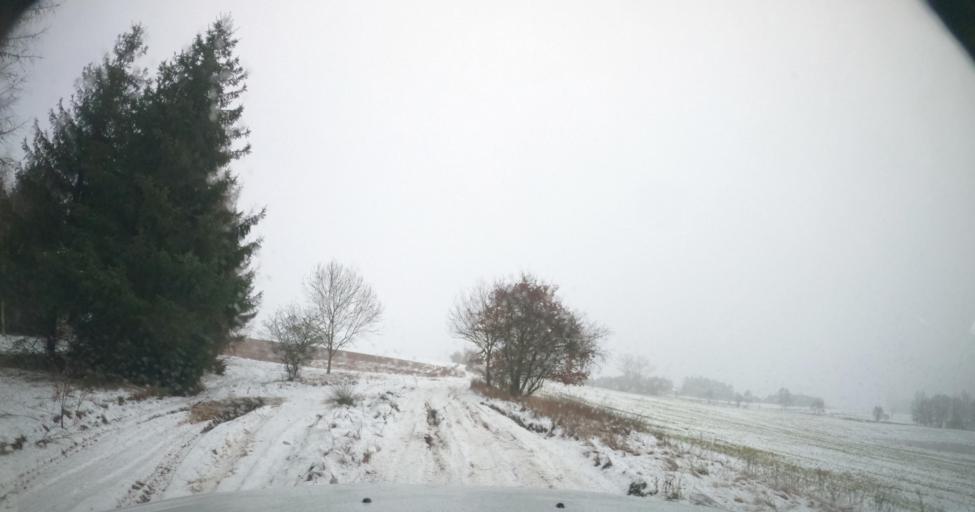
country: PL
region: West Pomeranian Voivodeship
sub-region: Powiat kamienski
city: Golczewo
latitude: 53.8706
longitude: 15.0577
